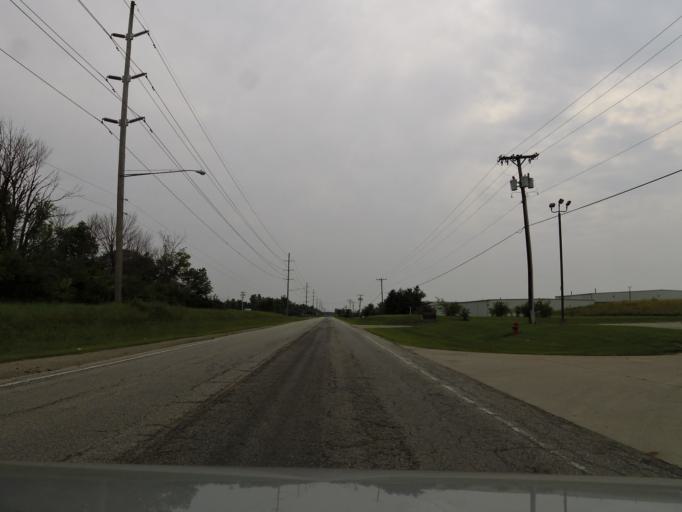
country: US
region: Ohio
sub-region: Clinton County
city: Wilmington
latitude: 39.4142
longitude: -83.8443
